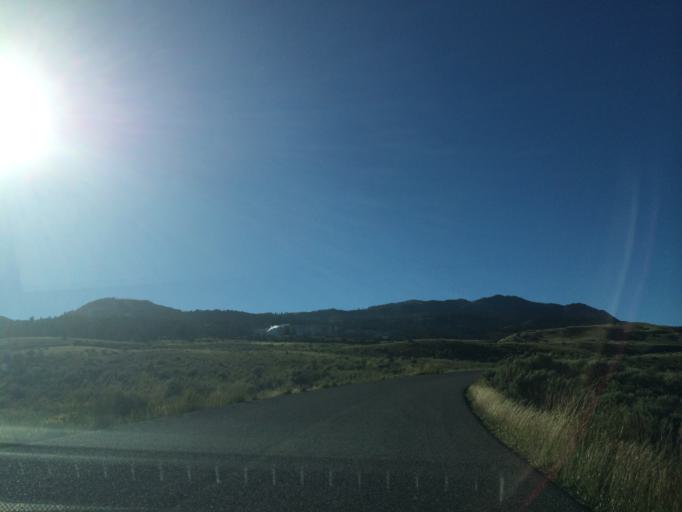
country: US
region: Montana
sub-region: Gallatin County
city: West Yellowstone
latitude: 44.9653
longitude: -110.6902
